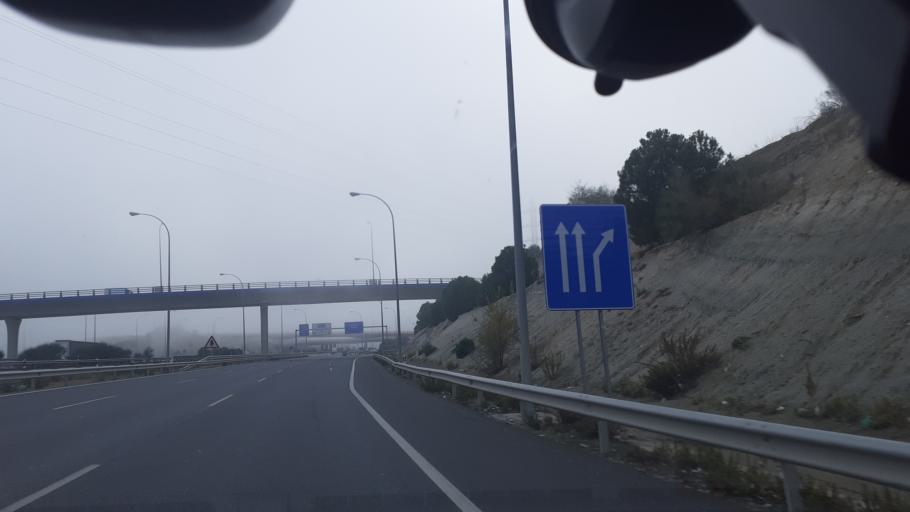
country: ES
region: Madrid
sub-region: Provincia de Madrid
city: Villa de Vallecas
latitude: 40.3771
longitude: -3.5928
